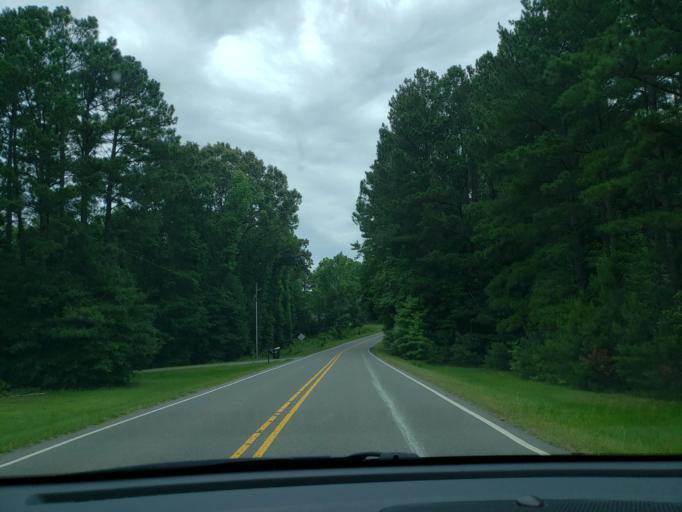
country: US
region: North Carolina
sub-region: Chatham County
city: Fearrington Village
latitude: 35.7645
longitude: -79.0067
